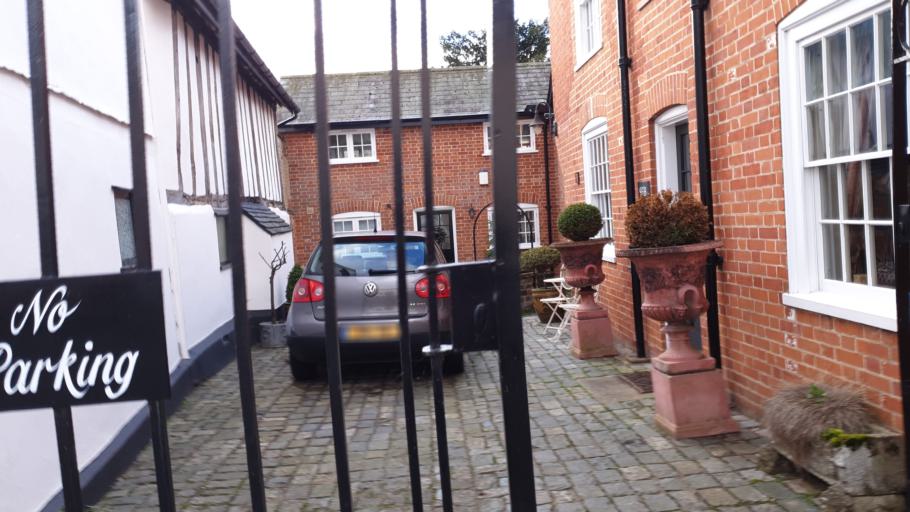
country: GB
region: England
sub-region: Suffolk
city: Hadleigh
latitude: 52.0451
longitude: 0.9527
